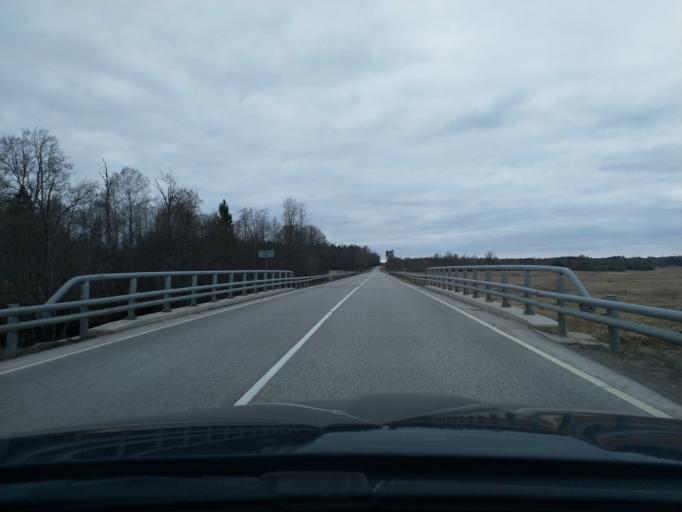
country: LV
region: Kuldigas Rajons
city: Kuldiga
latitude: 56.9664
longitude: 22.0590
